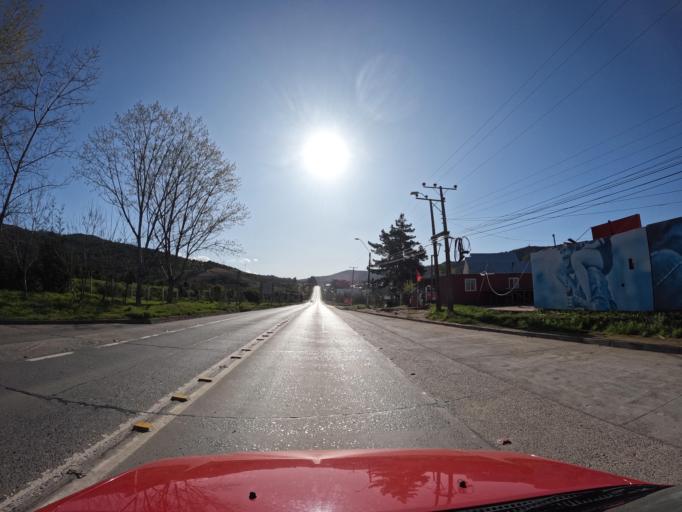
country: CL
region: Maule
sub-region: Provincia de Talca
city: Constitucion
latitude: -35.4508
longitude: -72.2803
